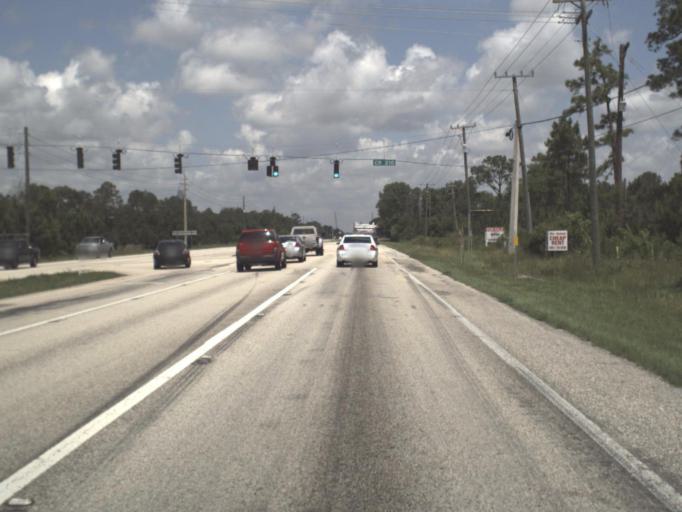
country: US
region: Florida
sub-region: Saint Johns County
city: Palm Valley
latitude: 30.0804
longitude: -81.4541
